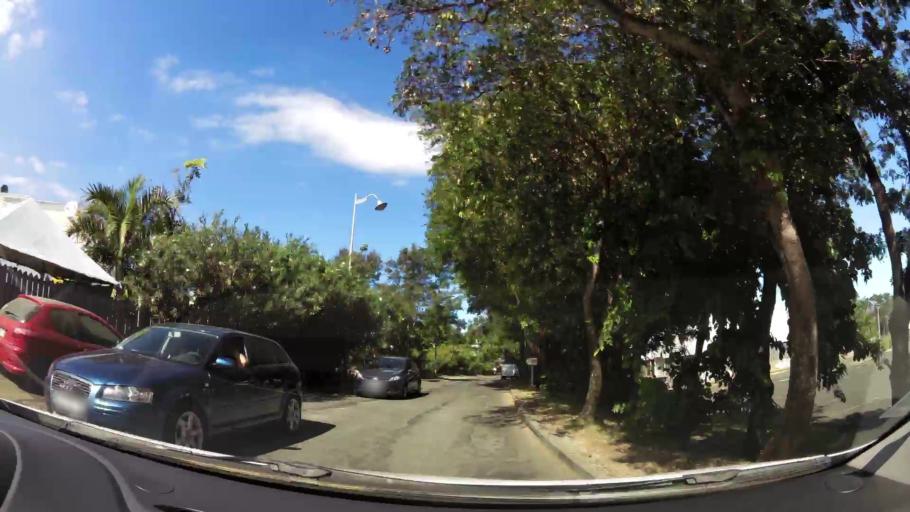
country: RE
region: Reunion
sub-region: Reunion
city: Saint-Pierre
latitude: -21.3256
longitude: 55.4768
